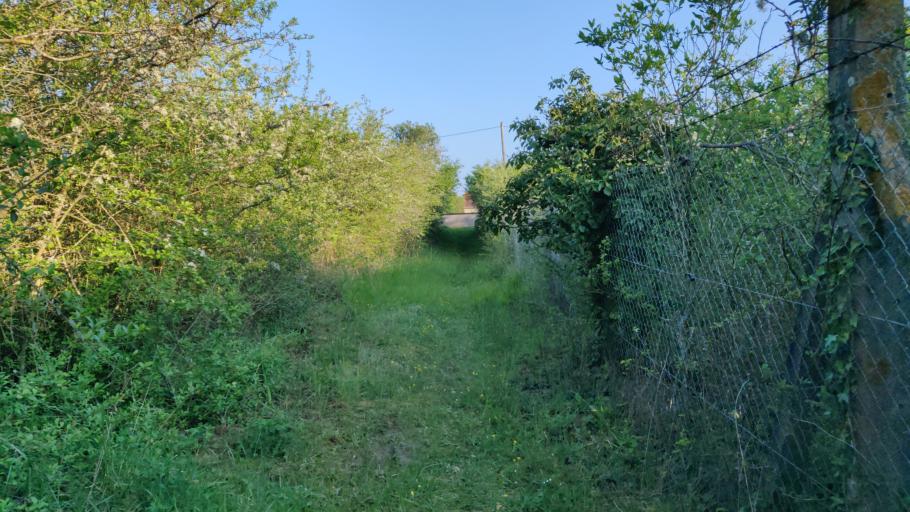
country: FR
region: Ile-de-France
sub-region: Departement des Yvelines
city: Freneuse
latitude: 49.0447
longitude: 1.6478
